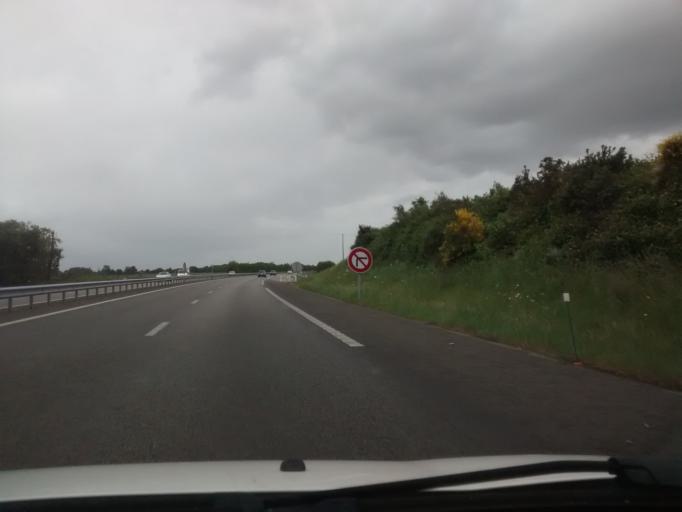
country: FR
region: Brittany
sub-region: Departement d'Ille-et-Vilaine
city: Plelan-le-Grand
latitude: 47.9736
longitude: -2.0974
